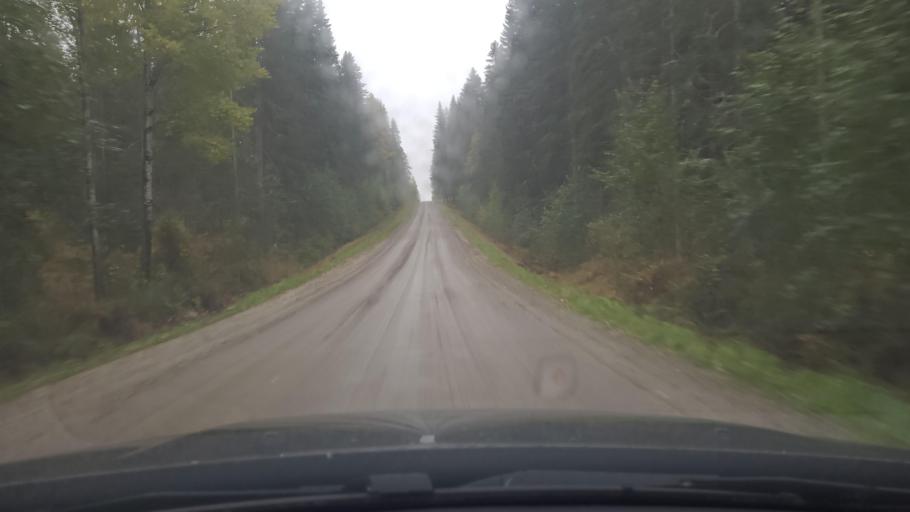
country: FI
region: Northern Savo
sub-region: Varkaus
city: Kangaslampi
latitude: 62.4504
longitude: 28.2948
